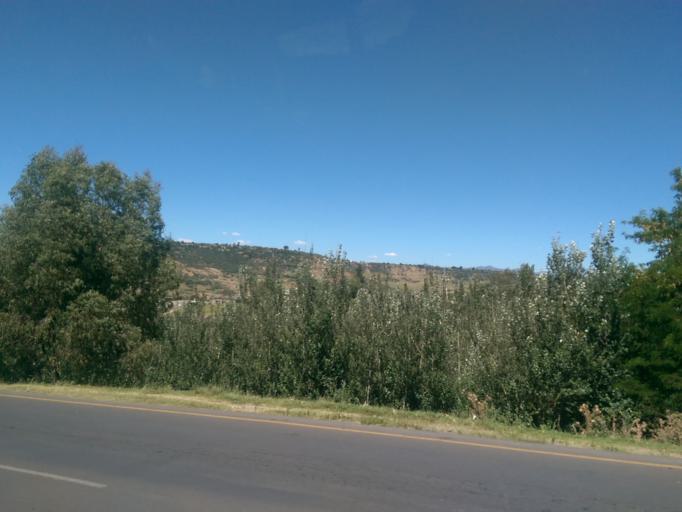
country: LS
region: Maseru
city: Maseru
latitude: -29.4110
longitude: 27.5593
